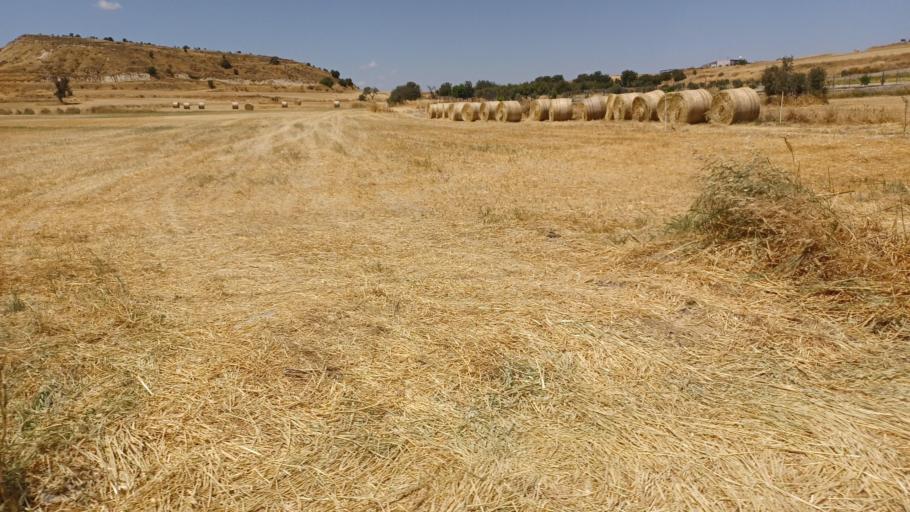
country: CY
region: Larnaka
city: Athienou
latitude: 35.0413
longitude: 33.5387
